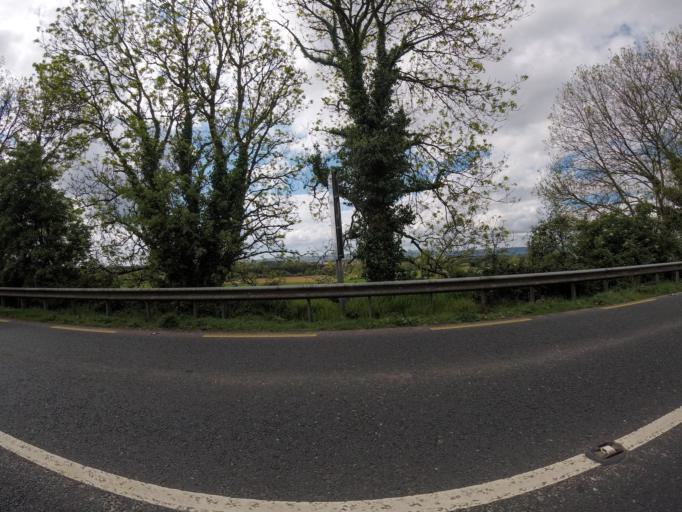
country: IE
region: Munster
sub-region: Waterford
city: Dungarvan
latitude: 52.1145
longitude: -7.5696
